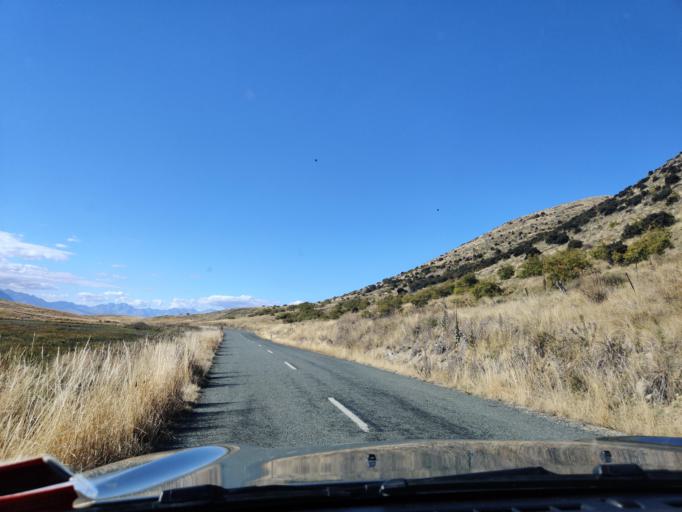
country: NZ
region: Canterbury
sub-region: Timaru District
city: Pleasant Point
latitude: -43.9788
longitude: 170.4627
